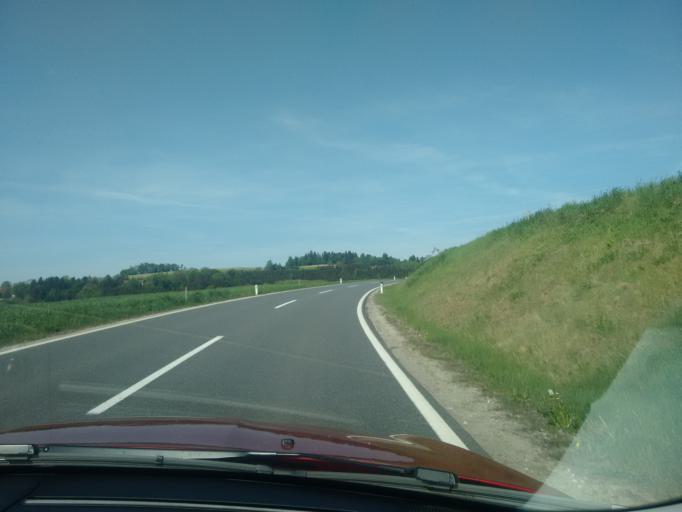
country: AT
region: Upper Austria
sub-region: Politischer Bezirk Grieskirchen
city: Grieskirchen
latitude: 48.3390
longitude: 13.8071
